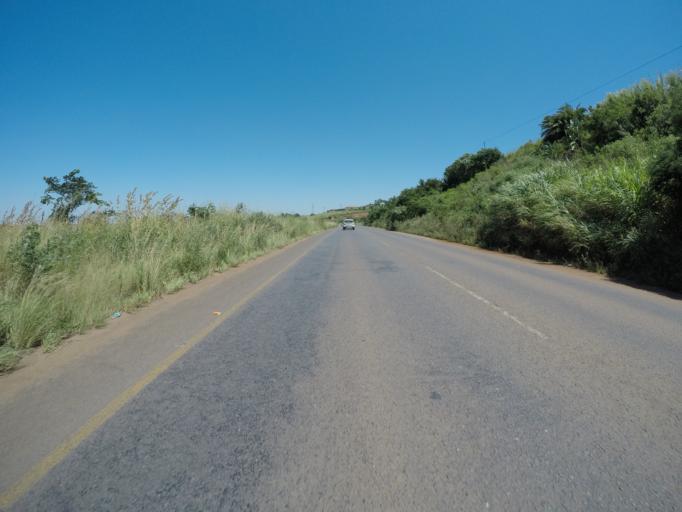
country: ZA
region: KwaZulu-Natal
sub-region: uThungulu District Municipality
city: Empangeni
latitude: -28.7540
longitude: 31.8755
